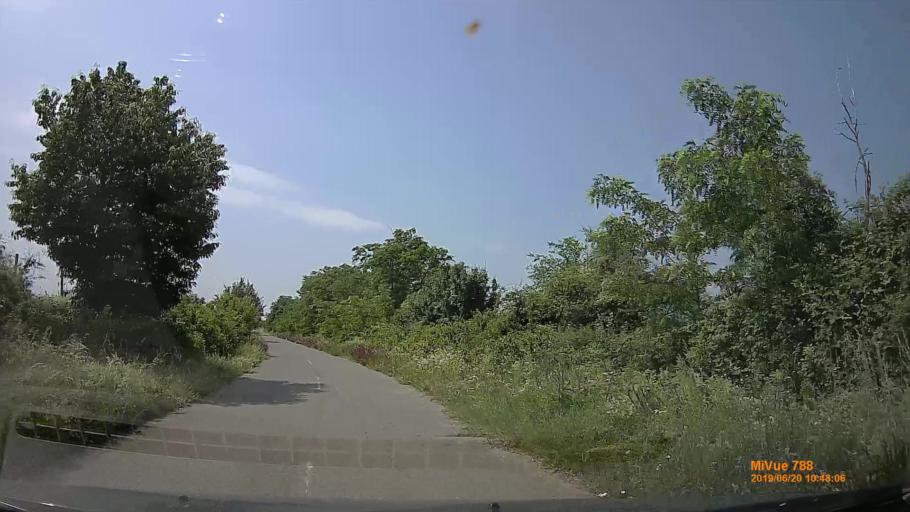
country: HU
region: Baranya
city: Hidas
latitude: 46.1720
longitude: 18.5823
